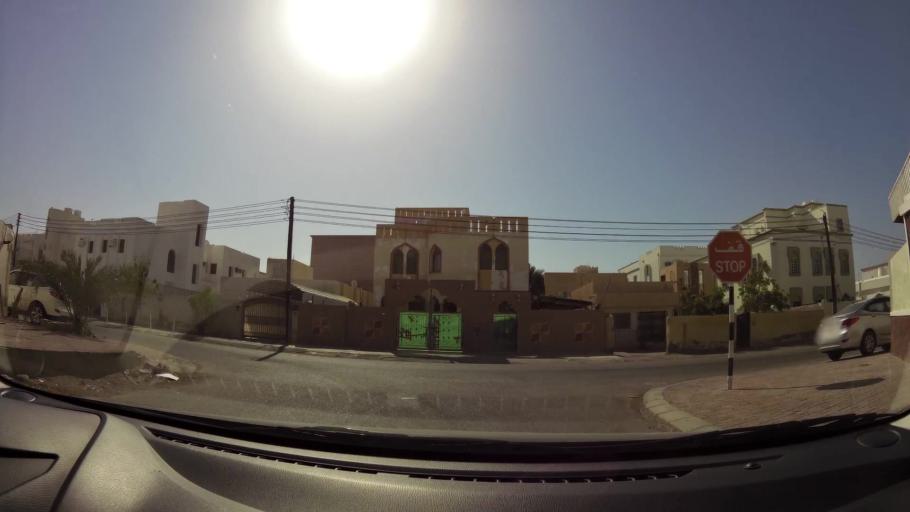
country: OM
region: Muhafazat Masqat
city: As Sib al Jadidah
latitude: 23.6284
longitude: 58.2007
